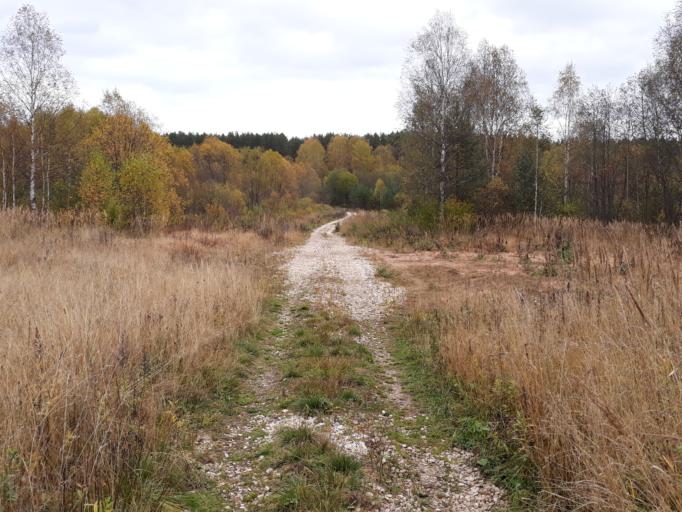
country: RU
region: Nizjnij Novgorod
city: Varnavino
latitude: 57.7138
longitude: 45.0247
